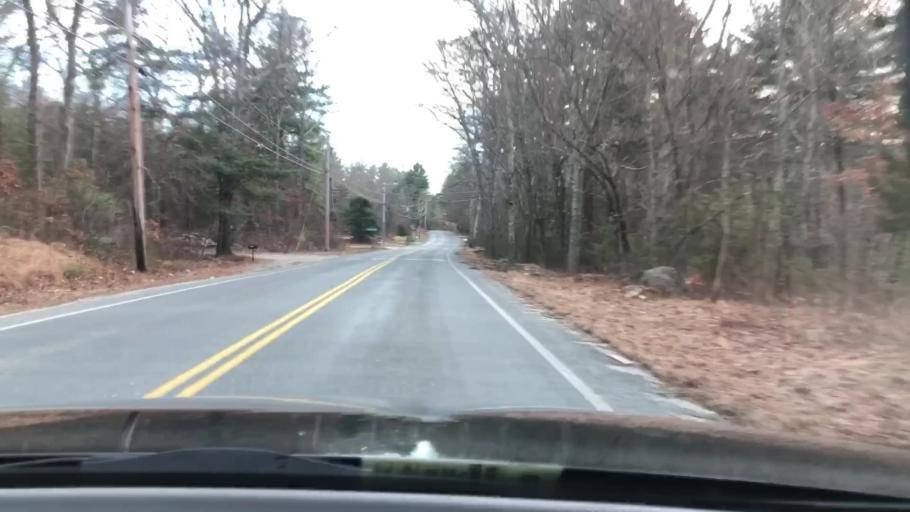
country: US
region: Massachusetts
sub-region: Worcester County
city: Mendon
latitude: 42.0730
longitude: -71.5251
